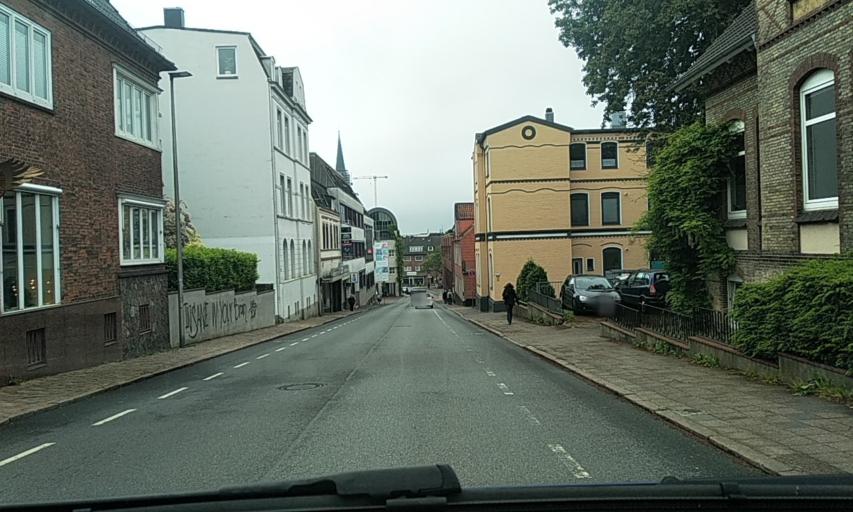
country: DE
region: Schleswig-Holstein
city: Schleswig
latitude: 54.5181
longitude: 9.5646
